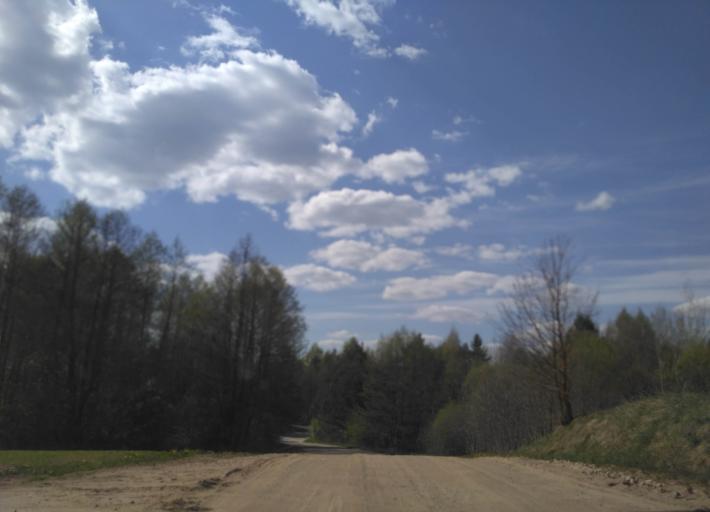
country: BY
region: Minsk
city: Narach
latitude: 54.9728
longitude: 26.6289
